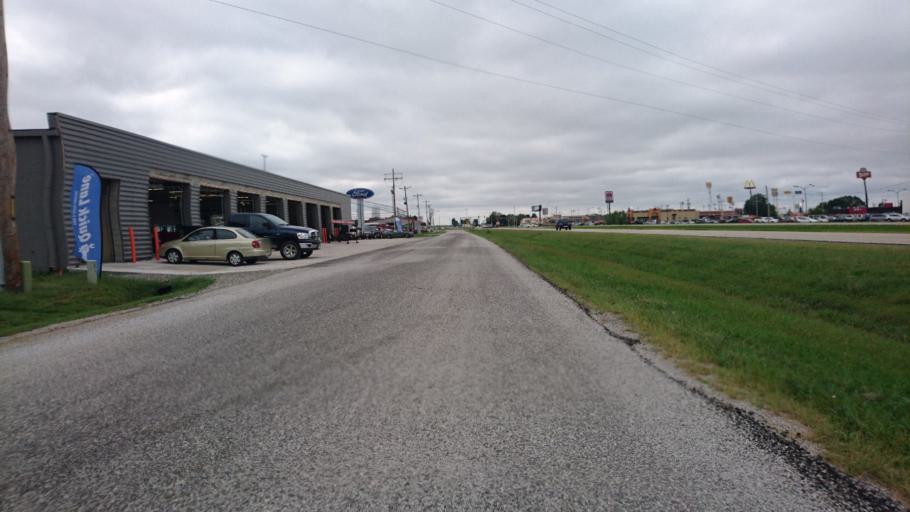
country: US
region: Illinois
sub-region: Montgomery County
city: Litchfield
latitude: 39.1812
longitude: -89.6671
